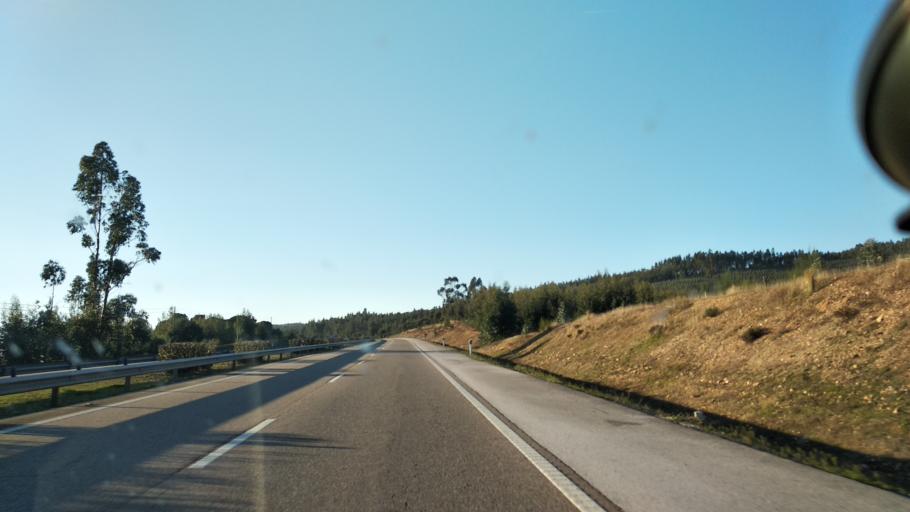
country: PT
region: Santarem
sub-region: Constancia
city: Constancia
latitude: 39.4906
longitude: -8.2939
